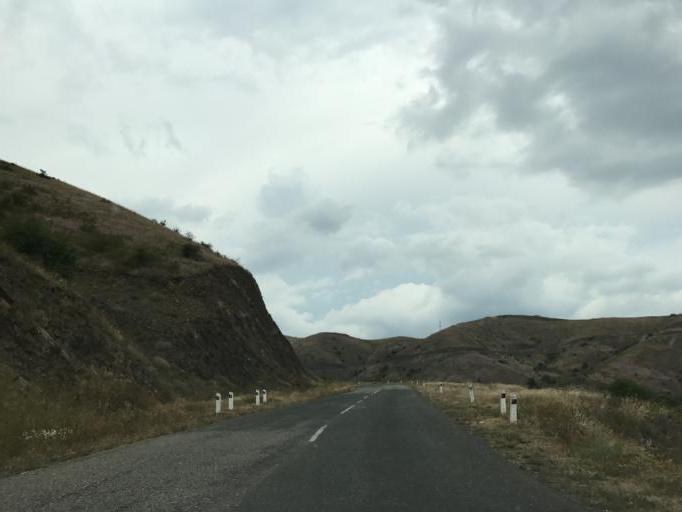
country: AZ
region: Lacin
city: Lacin
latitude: 39.6849
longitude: 46.6422
